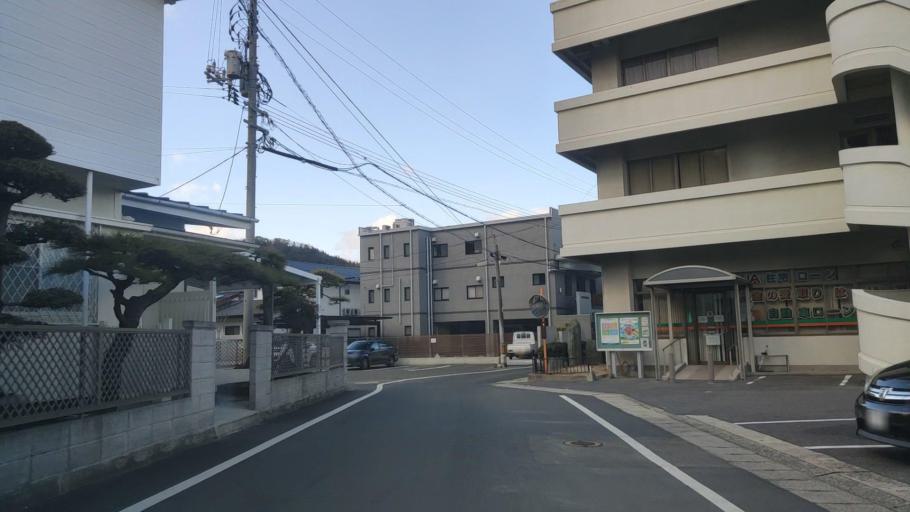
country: JP
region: Hiroshima
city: Innoshima
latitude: 34.2041
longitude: 133.1170
